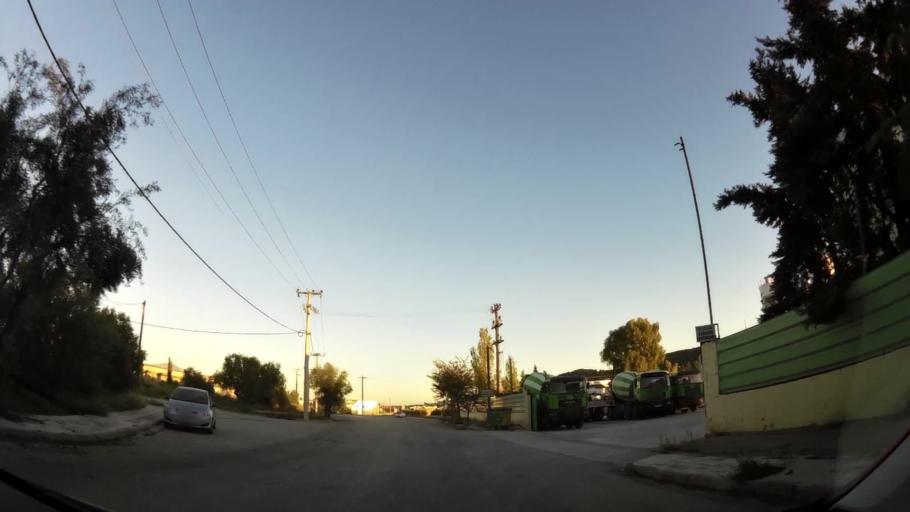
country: GR
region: Attica
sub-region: Nomarchia Dytikis Attikis
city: Ano Liosia
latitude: 38.0751
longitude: 23.6907
